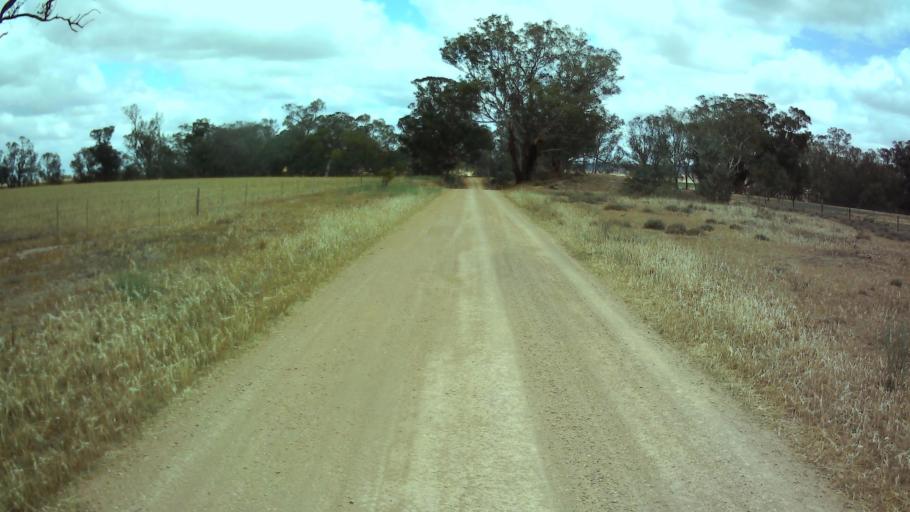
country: AU
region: New South Wales
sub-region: Weddin
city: Grenfell
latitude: -33.9794
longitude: 148.2679
